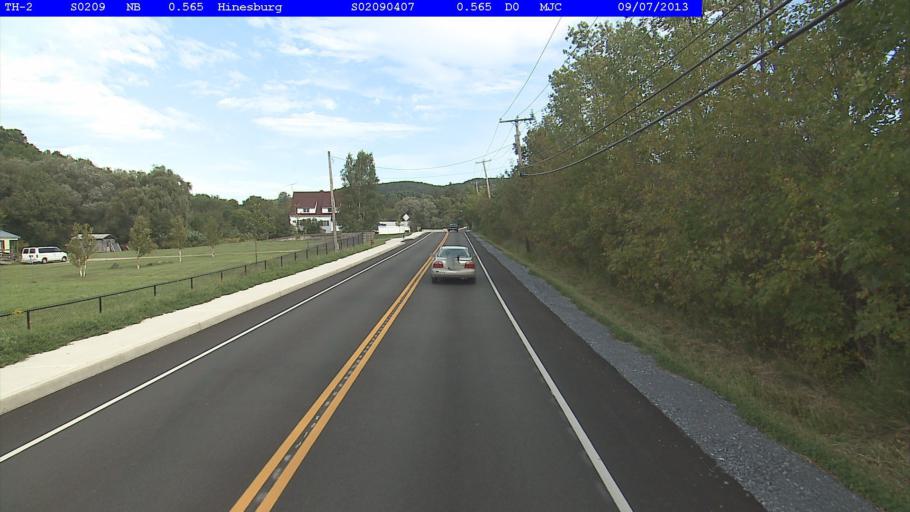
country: US
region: Vermont
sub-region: Chittenden County
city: Hinesburg
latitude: 44.3386
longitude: -73.1056
